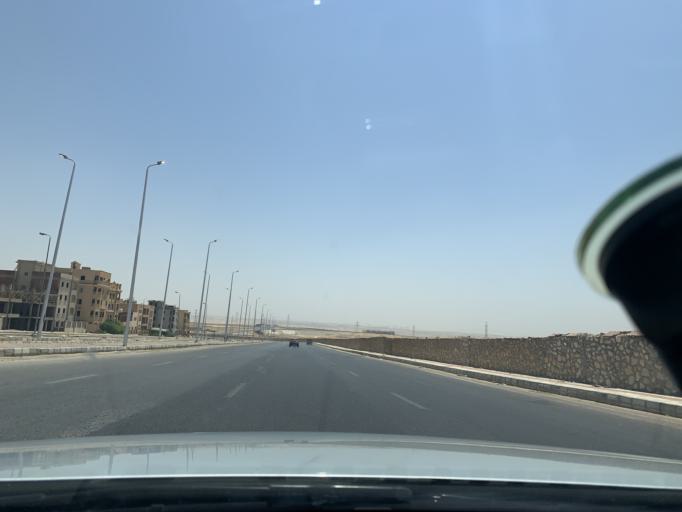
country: EG
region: Muhafazat al Qahirah
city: Halwan
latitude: 29.9818
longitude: 31.4686
